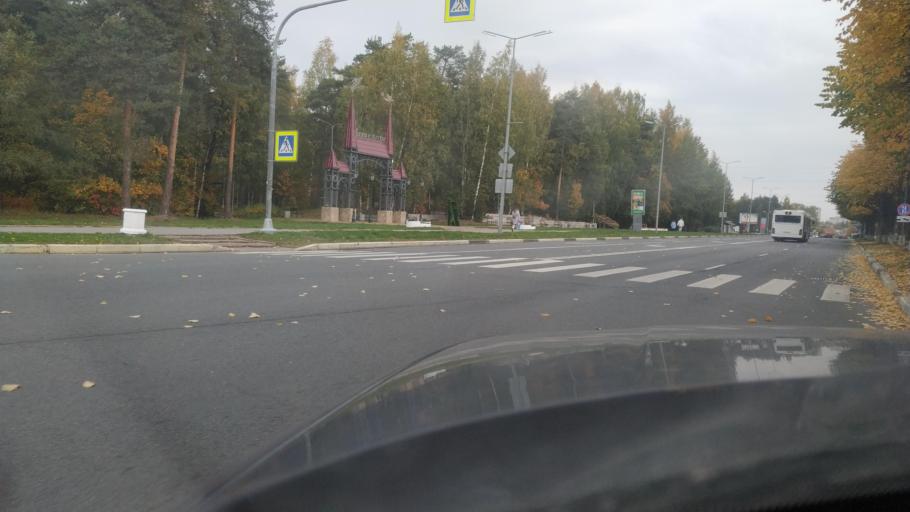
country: RU
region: Leningrad
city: Sosnovyy Bor
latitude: 59.8978
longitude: 29.0841
